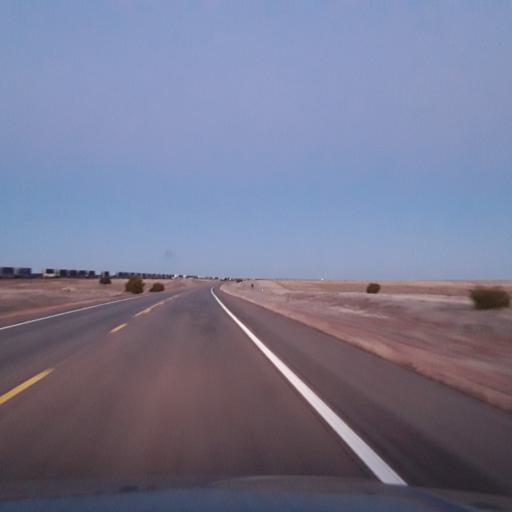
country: US
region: New Mexico
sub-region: Guadalupe County
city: Santa Rosa
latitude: 34.7465
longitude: -105.0165
